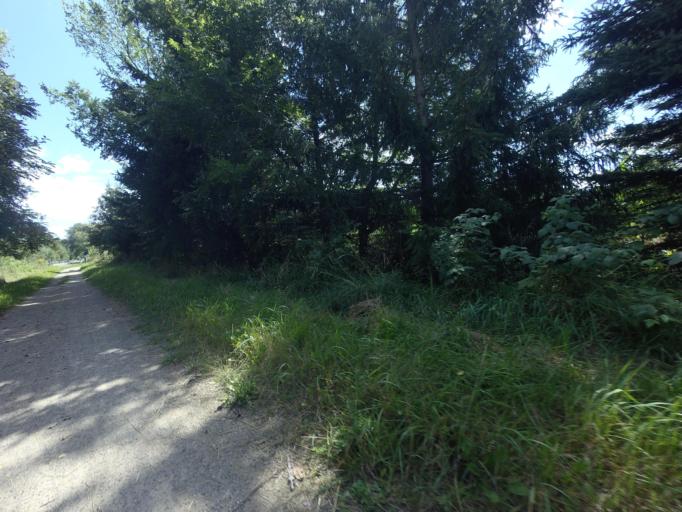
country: CA
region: Ontario
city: Orangeville
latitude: 43.7918
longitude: -80.2954
